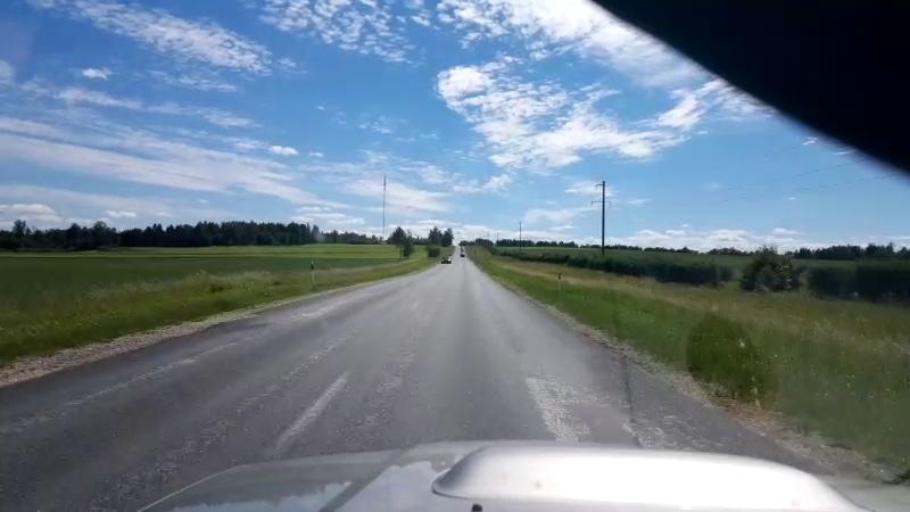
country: EE
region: Laeaene-Virumaa
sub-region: Rakke vald
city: Rakke
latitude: 58.8563
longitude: 26.2926
